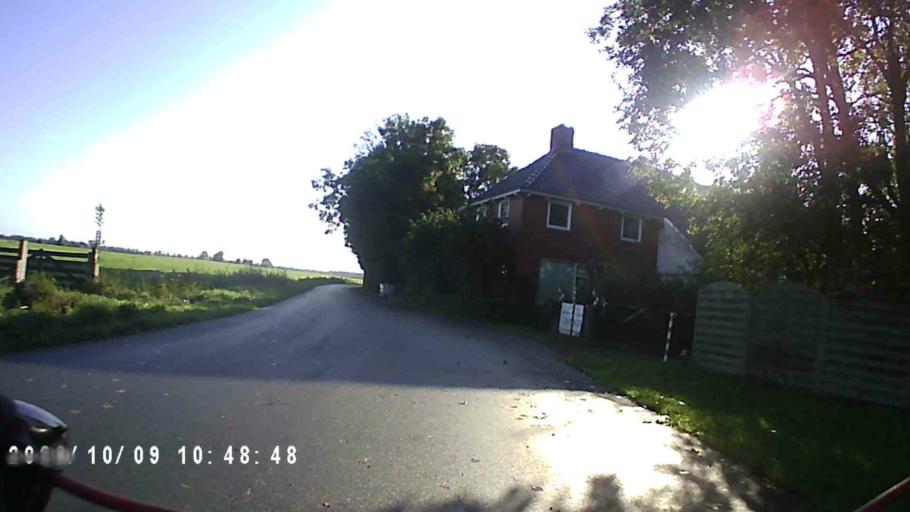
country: NL
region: Groningen
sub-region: Gemeente Groningen
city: Korrewegwijk
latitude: 53.2539
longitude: 6.5434
